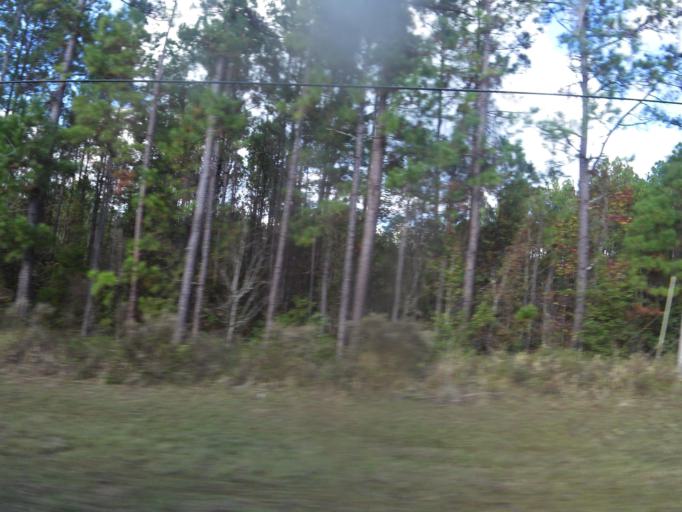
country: US
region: Florida
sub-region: Duval County
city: Baldwin
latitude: 30.1578
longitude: -81.9959
